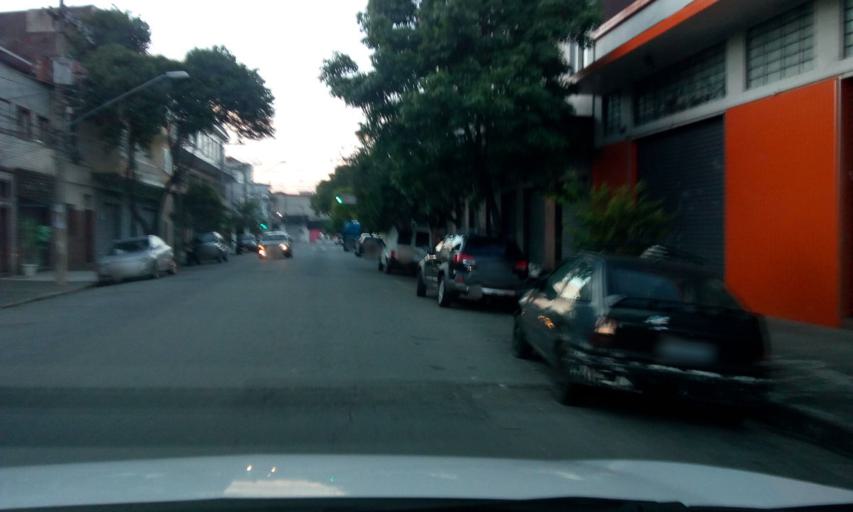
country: BR
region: Sao Paulo
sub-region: Sao Paulo
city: Sao Paulo
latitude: -23.5434
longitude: -46.6052
